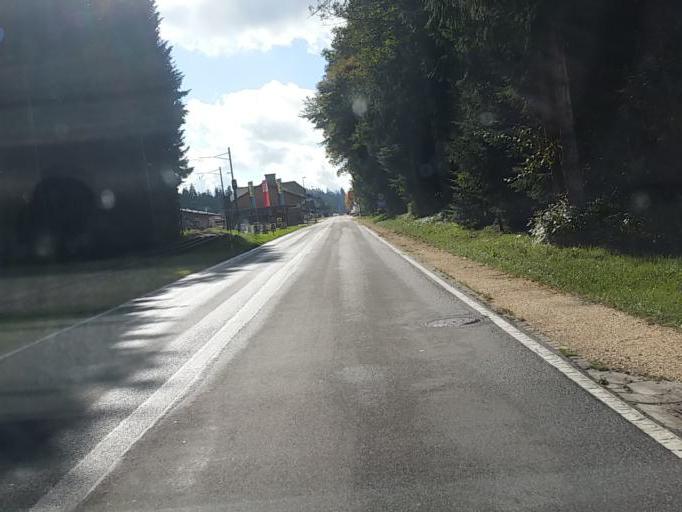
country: CH
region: Bern
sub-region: Emmental District
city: Sumiswald
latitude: 47.0647
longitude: 7.7491
